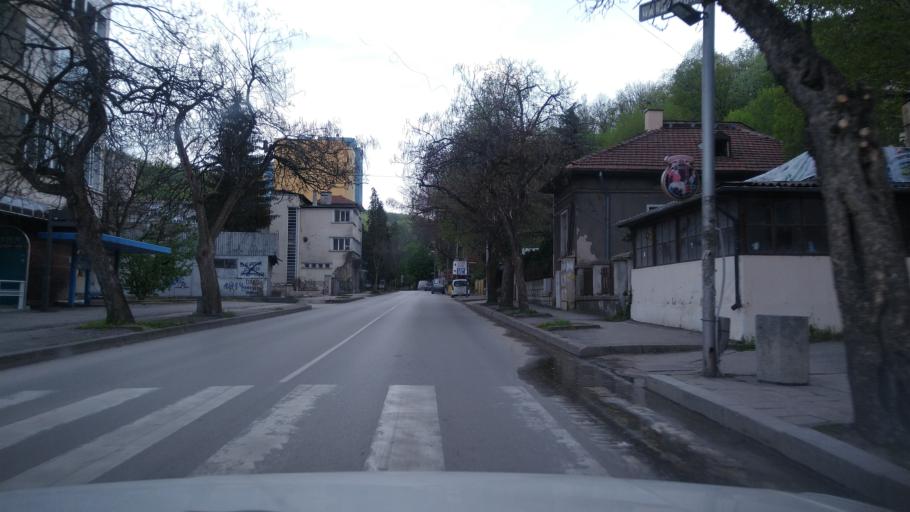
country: BG
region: Gabrovo
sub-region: Obshtina Gabrovo
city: Gabrovo
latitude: 42.8712
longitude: 25.3131
